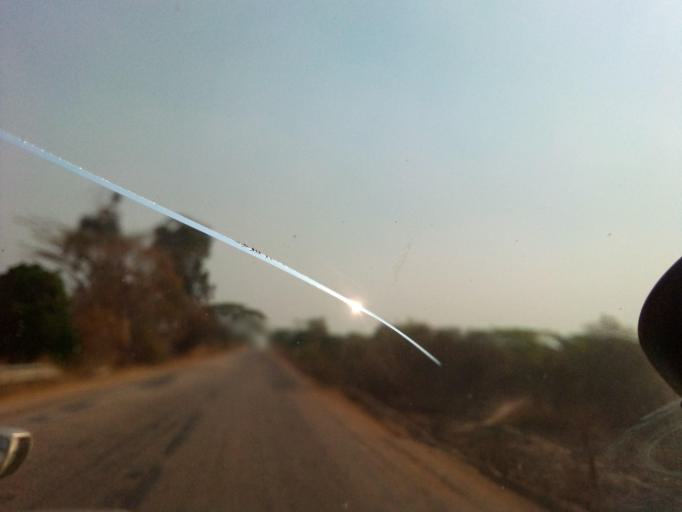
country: ZM
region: Northern
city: Chinsali
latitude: -10.9339
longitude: 32.0420
